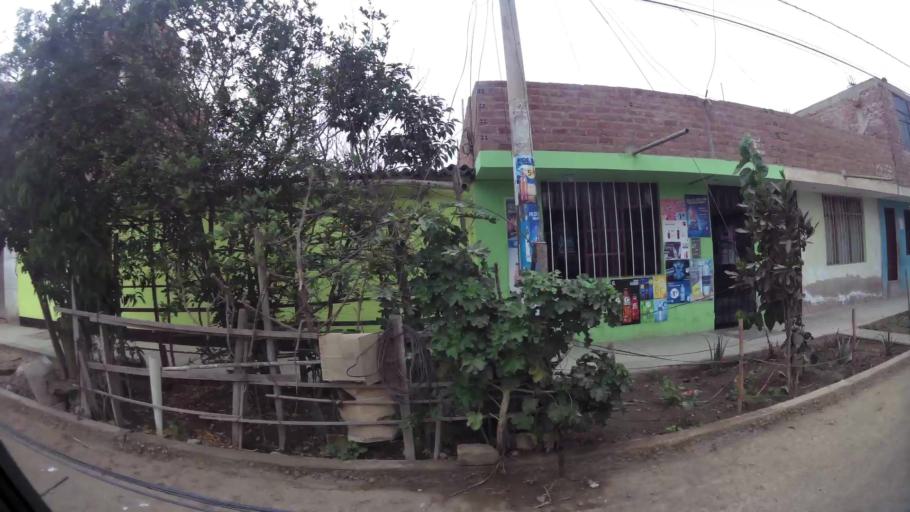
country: PE
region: La Libertad
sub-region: Provincia de Trujillo
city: Buenos Aires
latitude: -8.1423
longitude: -79.0490
